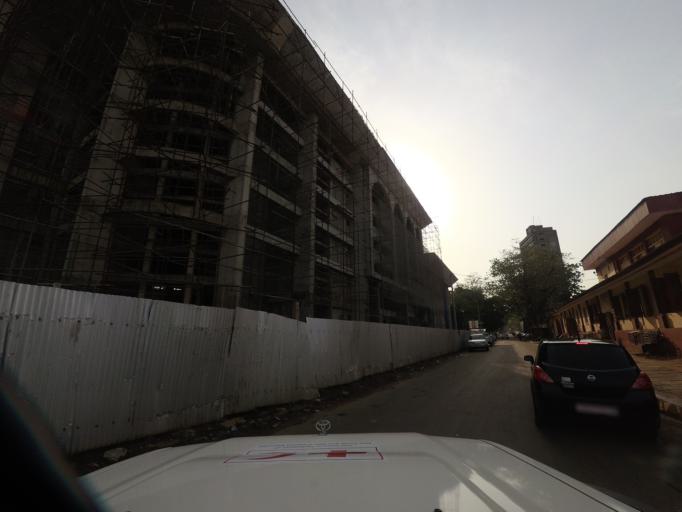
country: GN
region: Conakry
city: Camayenne
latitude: 9.5120
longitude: -13.7183
